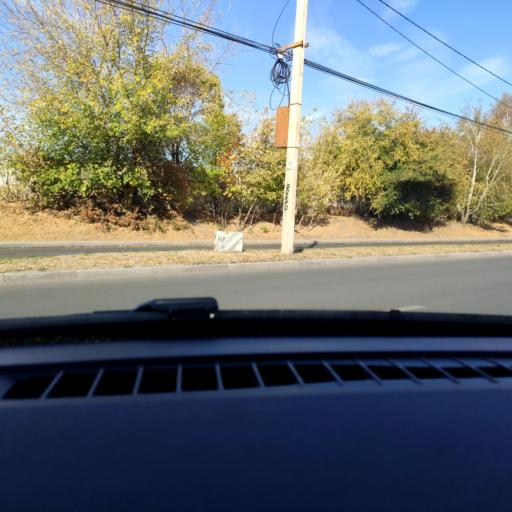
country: RU
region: Voronezj
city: Voronezh
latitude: 51.7074
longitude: 39.1956
